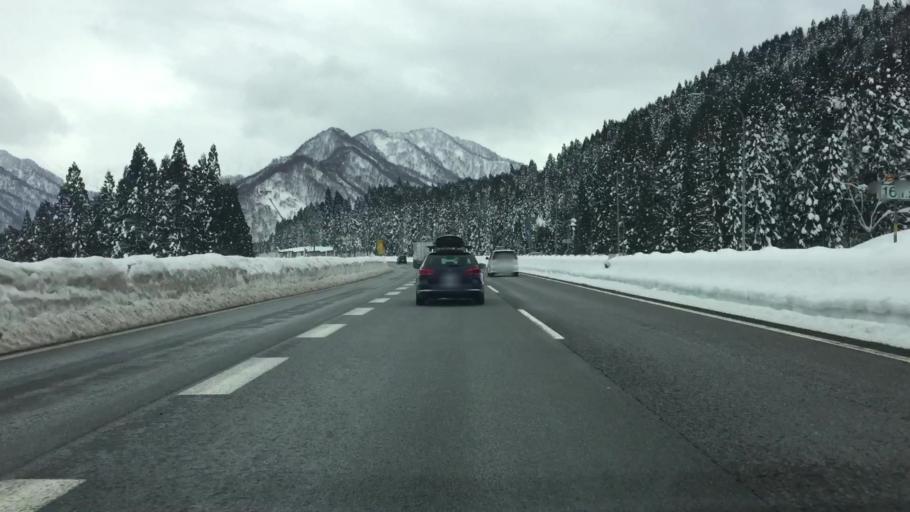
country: JP
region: Niigata
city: Shiozawa
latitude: 36.8893
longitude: 138.8484
